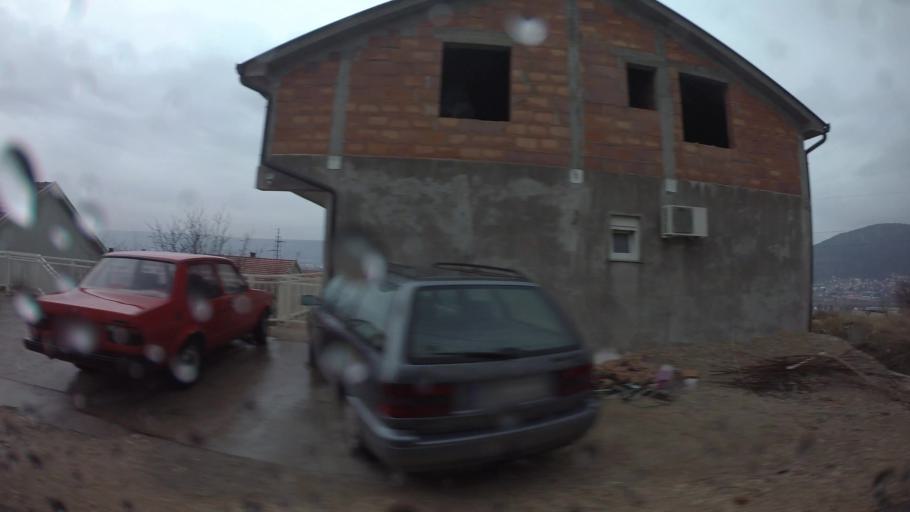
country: BA
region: Federation of Bosnia and Herzegovina
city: Rodoc
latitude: 43.3124
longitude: 17.8380
